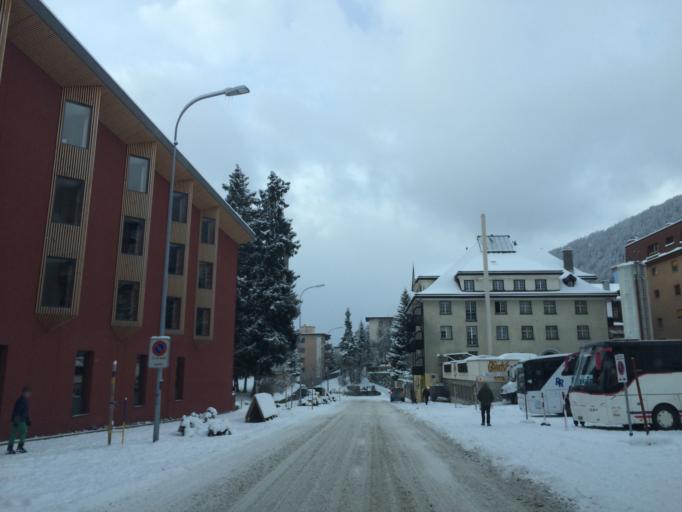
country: CH
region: Grisons
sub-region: Praettigau/Davos District
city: Davos
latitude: 46.7917
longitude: 9.8194
